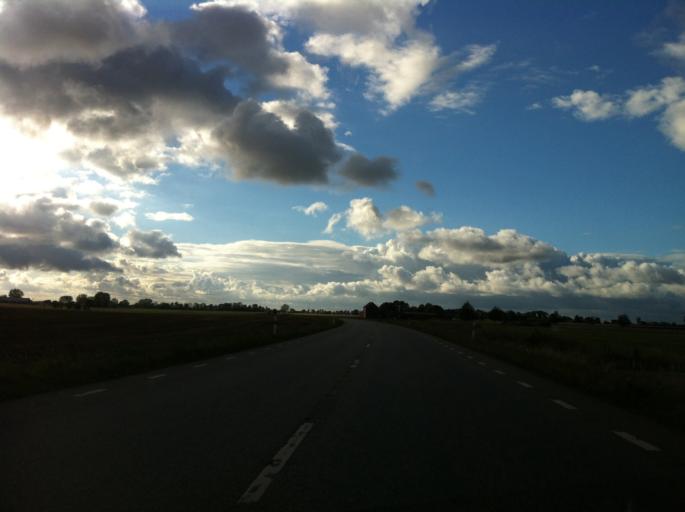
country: SE
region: Skane
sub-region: Svalovs Kommun
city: Teckomatorp
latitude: 55.8777
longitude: 13.0480
